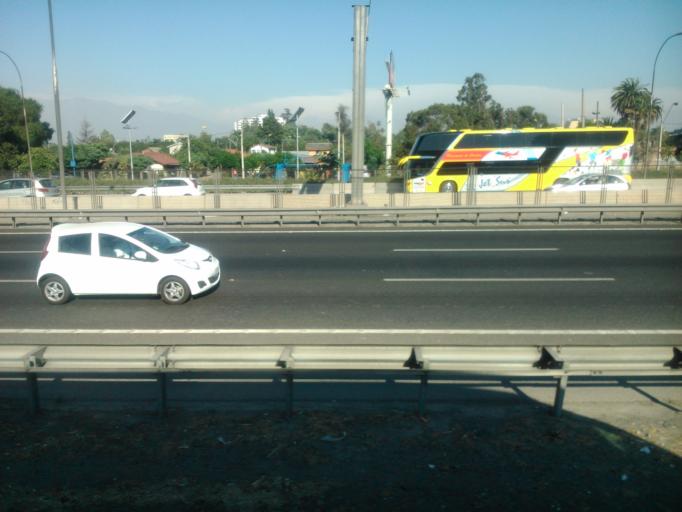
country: CL
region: Santiago Metropolitan
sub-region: Provincia de Maipo
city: San Bernardo
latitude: -33.5919
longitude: -70.7153
